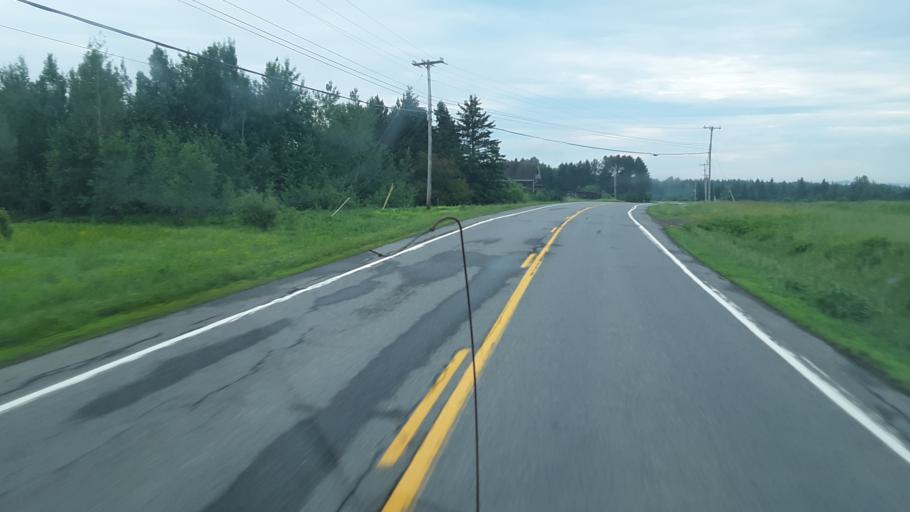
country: US
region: Maine
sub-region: Aroostook County
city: Presque Isle
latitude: 46.5950
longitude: -68.3878
